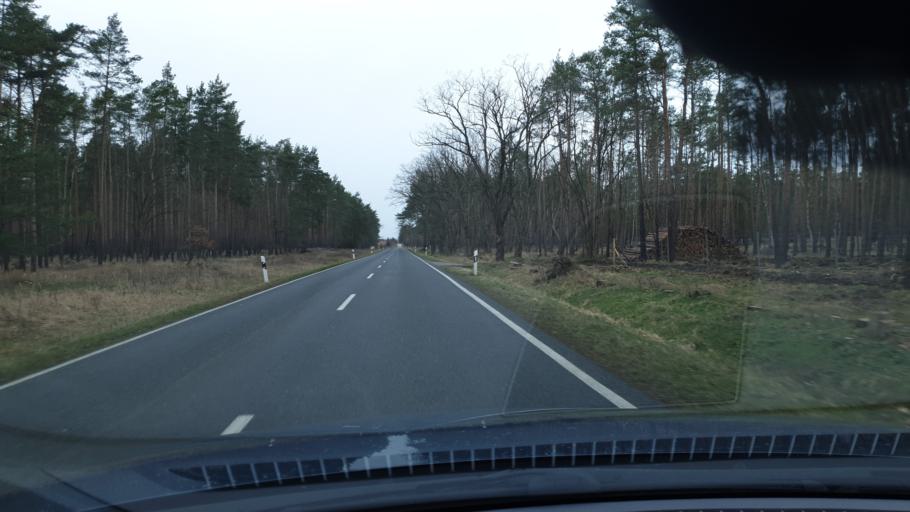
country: DE
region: Saxony-Anhalt
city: Radis
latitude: 51.7743
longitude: 12.4921
